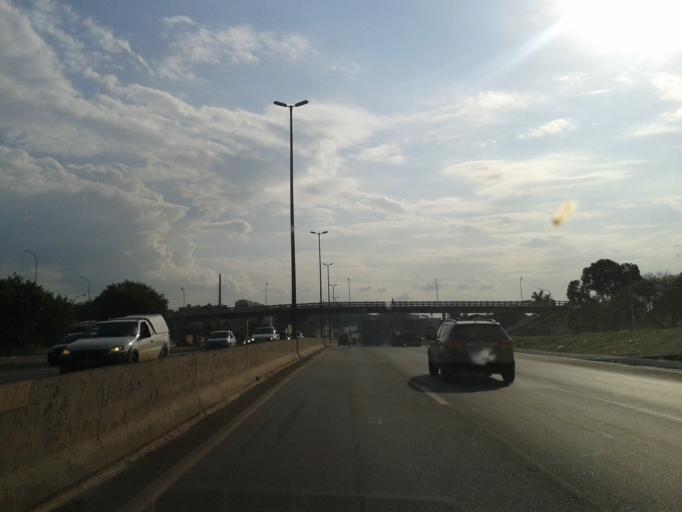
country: BR
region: Minas Gerais
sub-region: Belo Horizonte
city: Belo Horizonte
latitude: -19.8680
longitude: -43.9366
